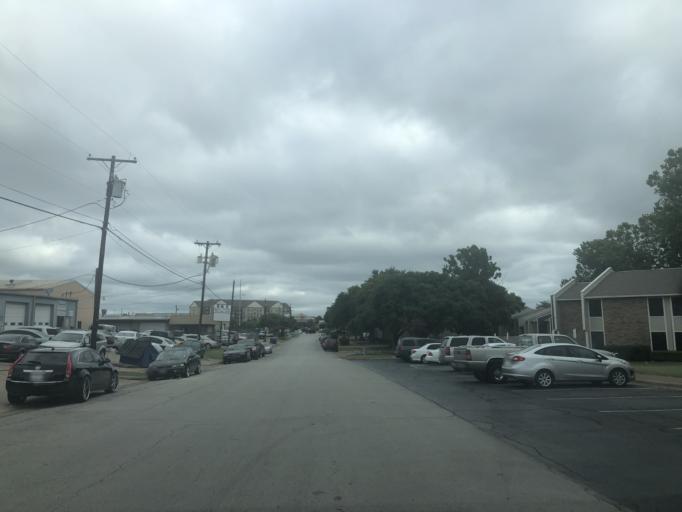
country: US
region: Texas
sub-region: Dallas County
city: Duncanville
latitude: 32.6594
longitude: -96.9059
